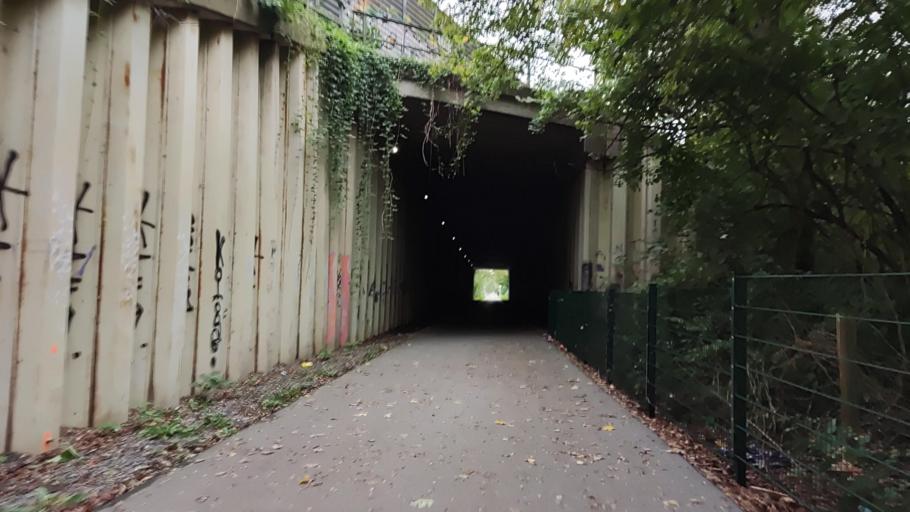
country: DE
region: North Rhine-Westphalia
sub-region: Regierungsbezirk Arnsberg
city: Herne
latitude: 51.5593
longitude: 7.2414
